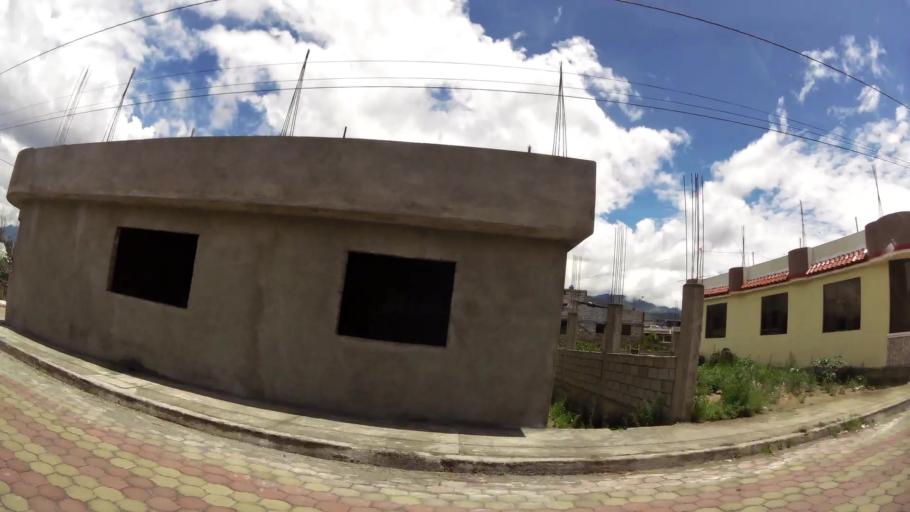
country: EC
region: Tungurahua
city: Pelileo
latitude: -1.3289
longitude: -78.5285
